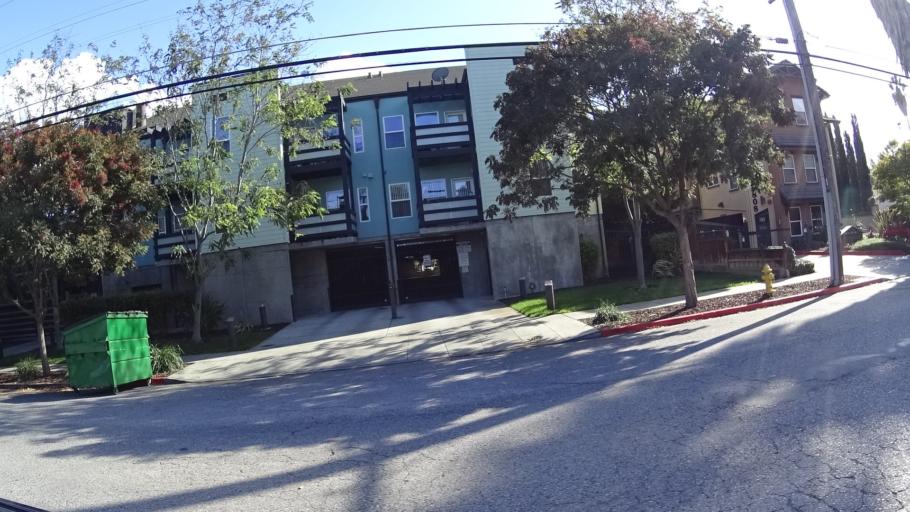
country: US
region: California
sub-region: Santa Clara County
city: San Jose
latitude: 37.3360
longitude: -121.9104
